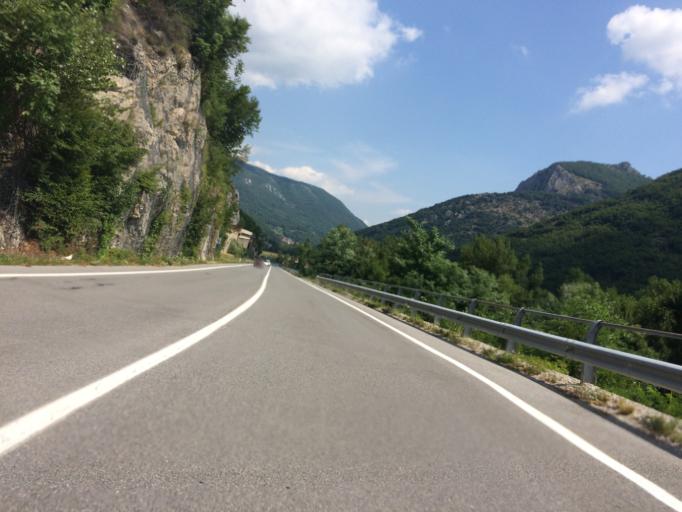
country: IT
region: Piedmont
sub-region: Provincia di Cuneo
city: Ormea
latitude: 44.1677
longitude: 7.9740
